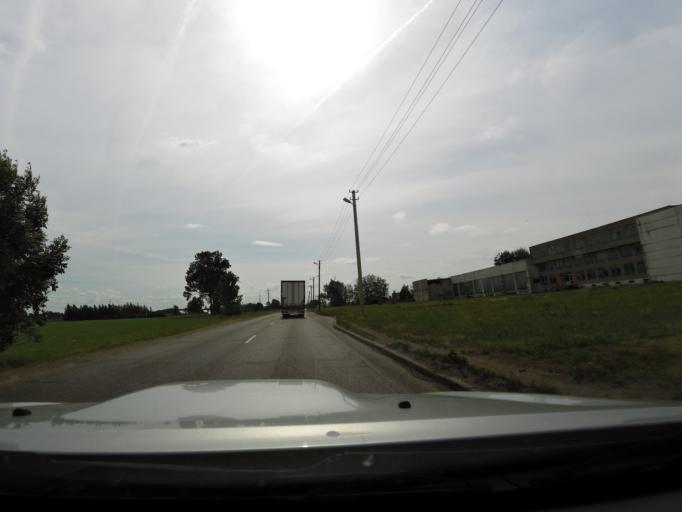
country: LT
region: Marijampoles apskritis
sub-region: Marijampole Municipality
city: Marijampole
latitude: 54.5686
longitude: 23.3915
